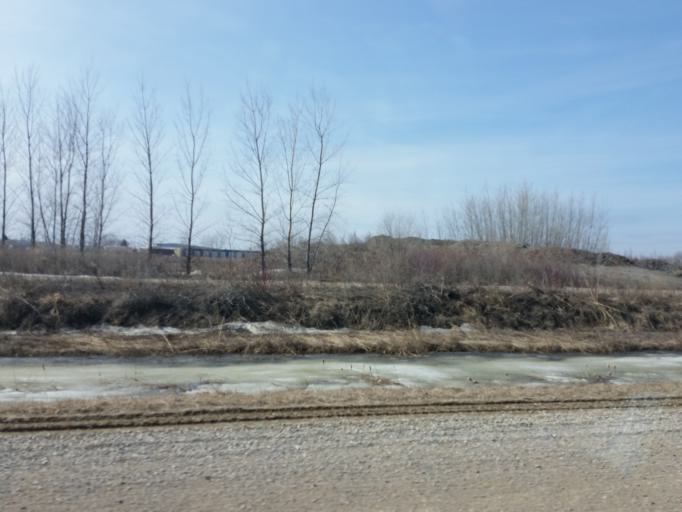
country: US
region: North Dakota
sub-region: Walsh County
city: Grafton
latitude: 48.4316
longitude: -97.4055
